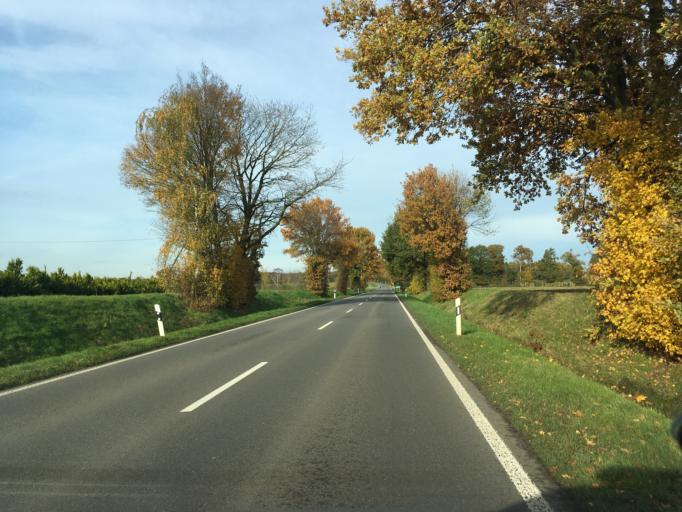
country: DE
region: North Rhine-Westphalia
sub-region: Regierungsbezirk Munster
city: Heiden
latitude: 51.8349
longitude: 6.9339
